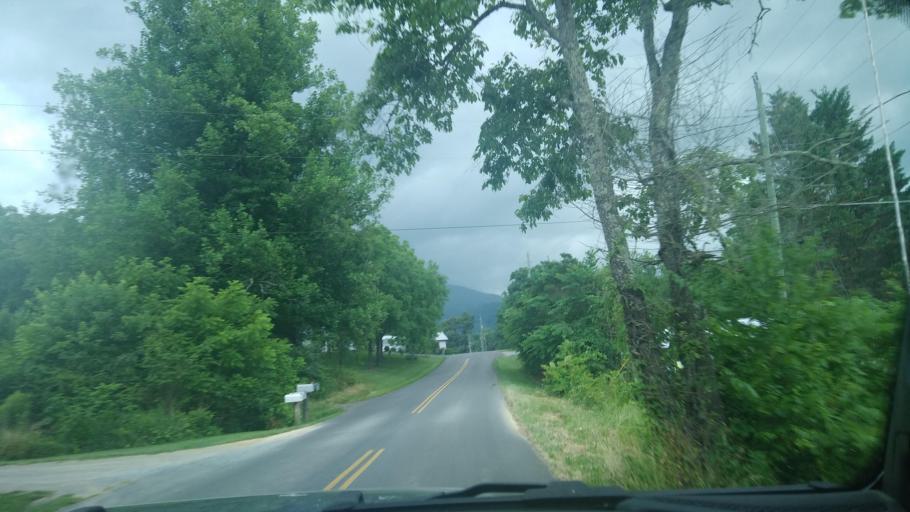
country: US
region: Tennessee
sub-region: Sevier County
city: Pigeon Forge
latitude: 35.7448
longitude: -83.6146
